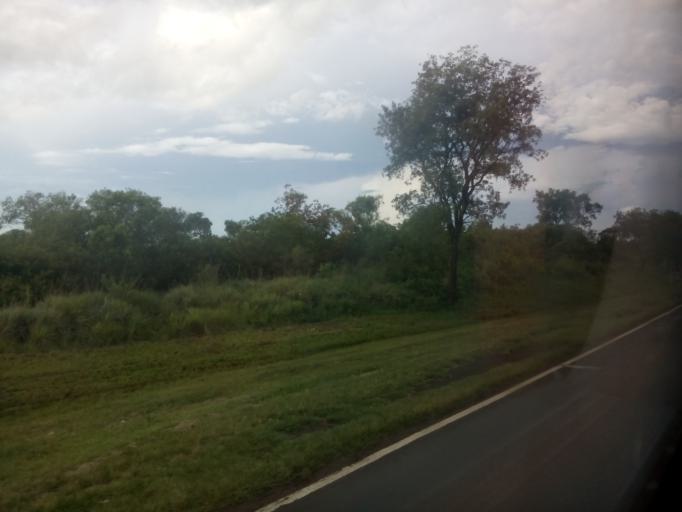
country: AR
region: Misiones
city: Santa Ana
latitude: -27.4269
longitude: -55.6268
